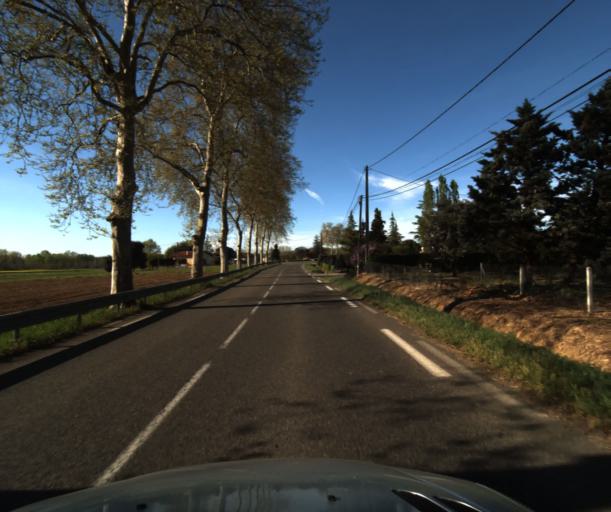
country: FR
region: Midi-Pyrenees
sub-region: Departement du Tarn-et-Garonne
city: Montbeton
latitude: 44.0664
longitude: 1.2868
